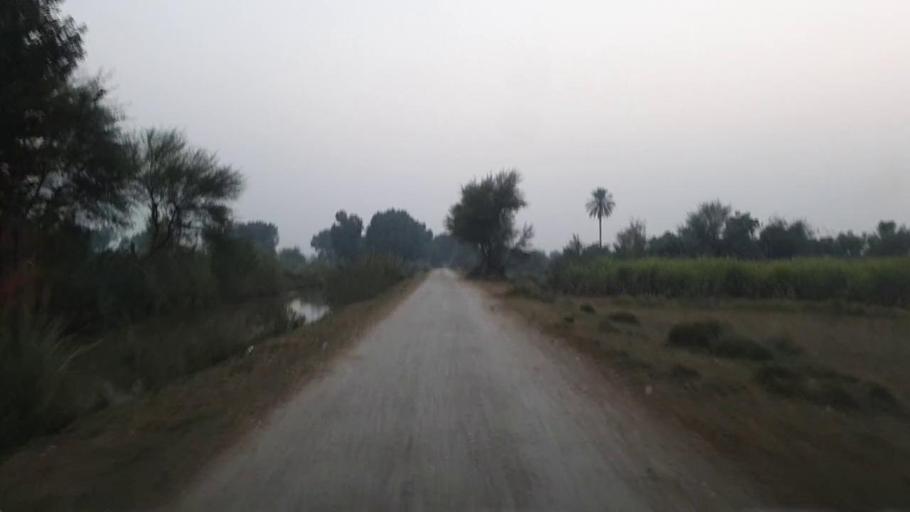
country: PK
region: Sindh
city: Karaundi
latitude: 26.9322
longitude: 68.4404
